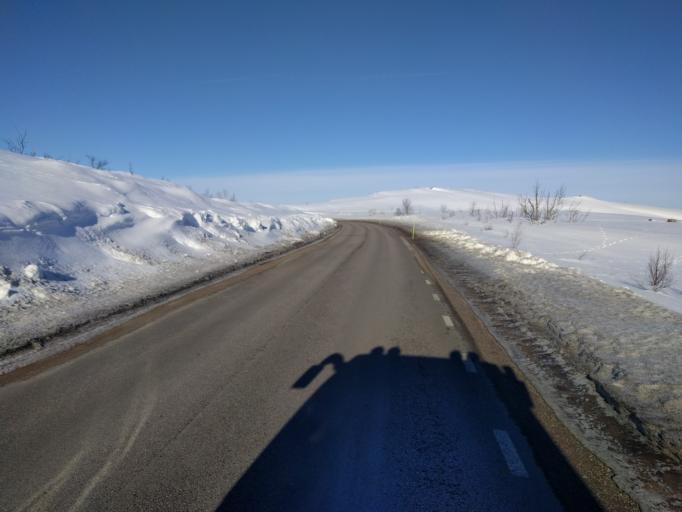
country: NO
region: Troms
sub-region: Bardu
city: Setermoen
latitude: 68.4305
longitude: 18.2052
